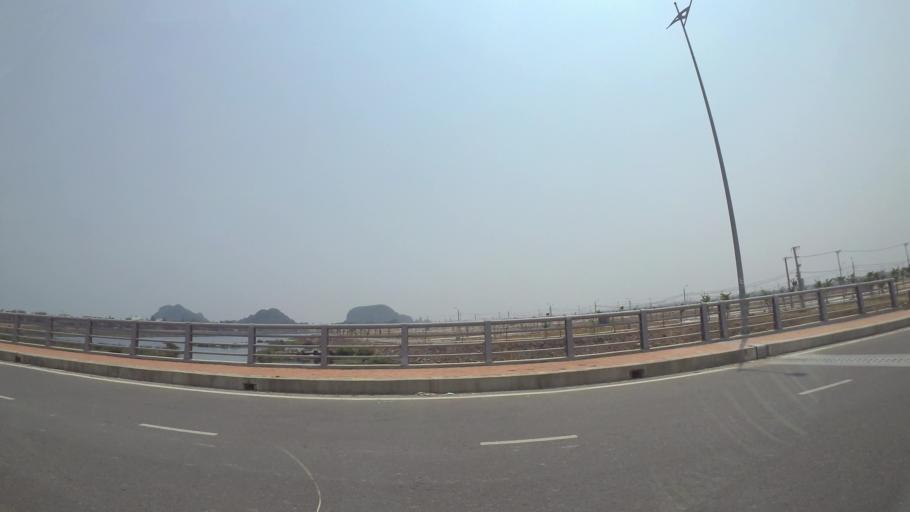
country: VN
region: Da Nang
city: Ngu Hanh Son
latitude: 16.0124
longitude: 108.2468
